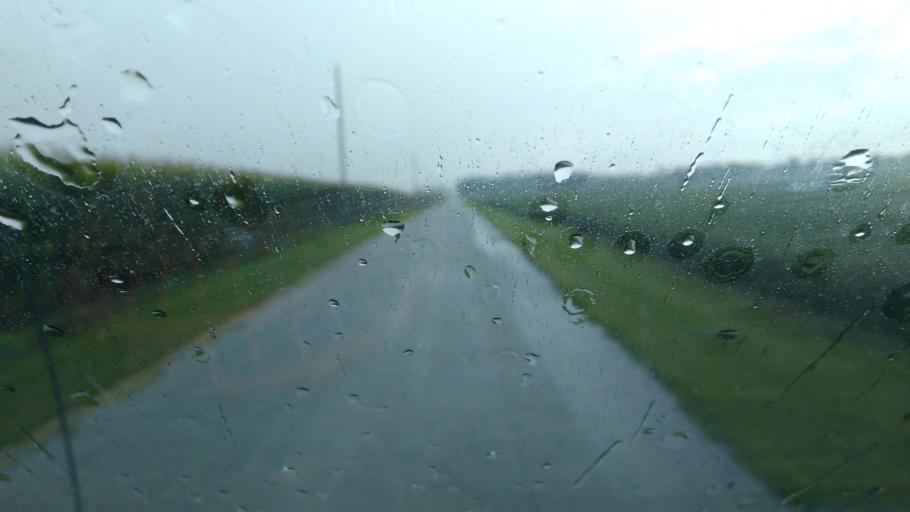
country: US
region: Ohio
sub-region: Hardin County
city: Kenton
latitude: 40.7169
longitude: -83.5670
